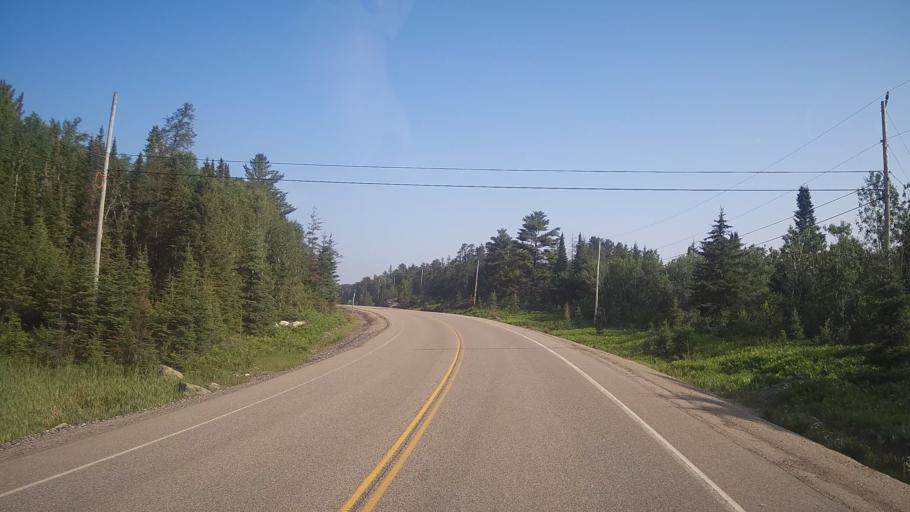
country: CA
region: Ontario
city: Rayside-Balfour
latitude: 46.7125
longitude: -81.5619
